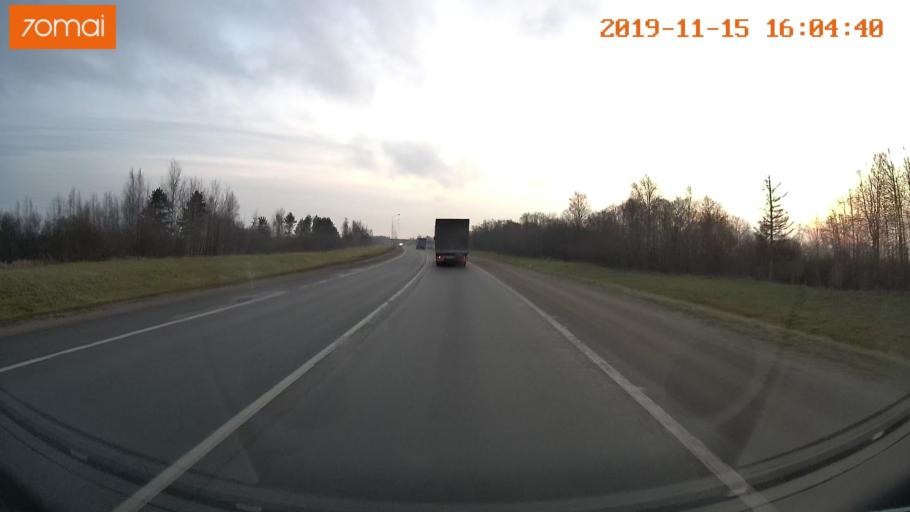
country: RU
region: Jaroslavl
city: Yaroslavl
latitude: 57.7454
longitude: 39.8990
